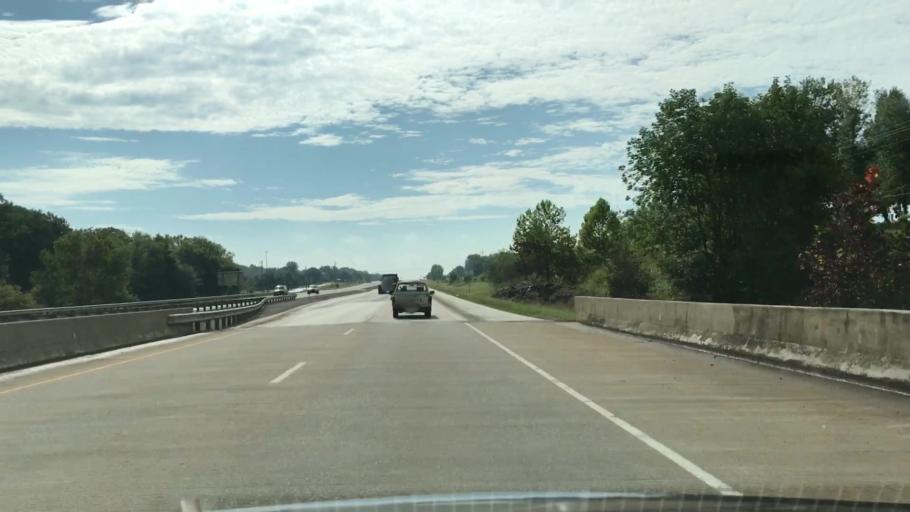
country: US
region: Kentucky
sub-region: Warren County
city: Plano
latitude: 36.8953
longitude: -86.3802
